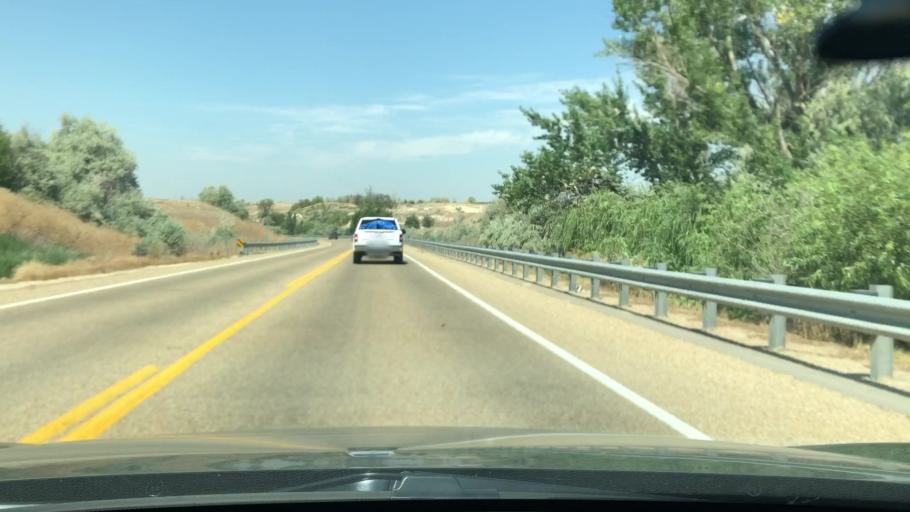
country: US
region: Idaho
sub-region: Canyon County
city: Wilder
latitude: 43.7157
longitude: -116.9118
